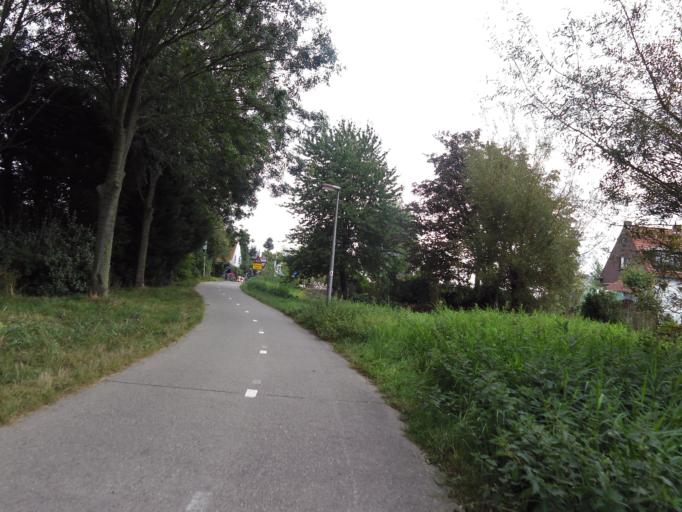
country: NL
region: South Holland
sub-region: Gemeente Rijnwoude
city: Benthuizen
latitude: 52.0749
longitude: 4.5345
